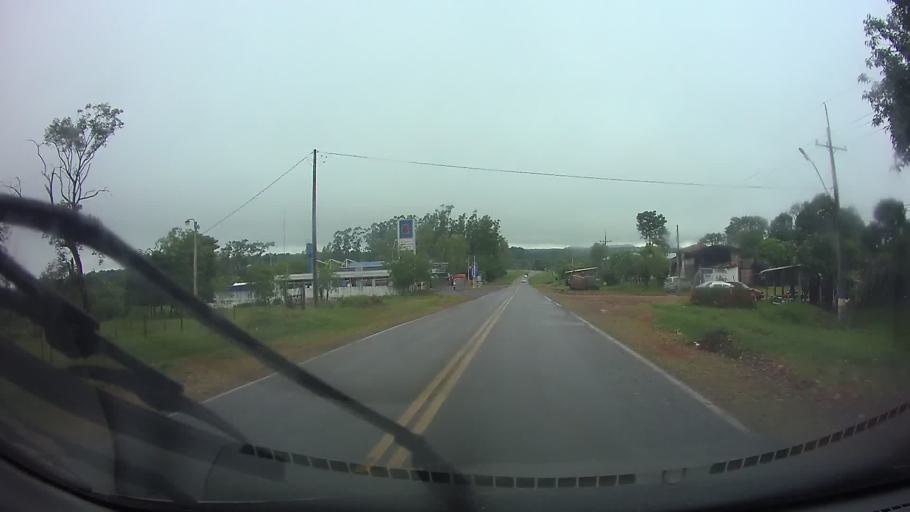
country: PY
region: Central
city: Ita
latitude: -25.5132
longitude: -57.3555
